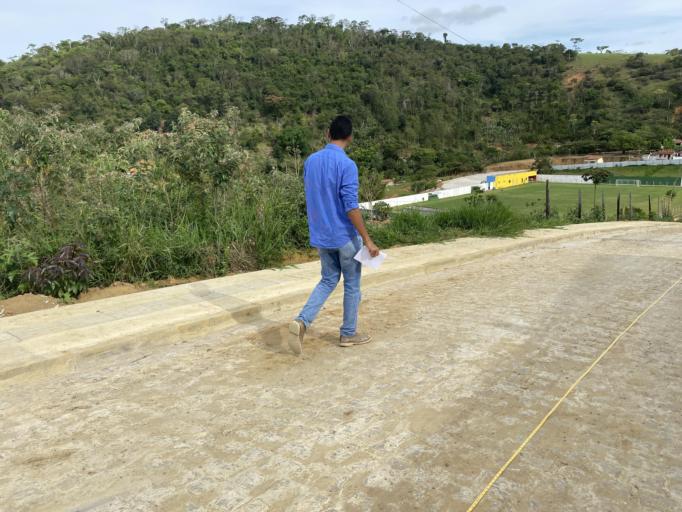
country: BR
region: Bahia
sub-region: Mutuipe
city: Mutuipe
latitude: -13.2562
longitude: -39.5649
